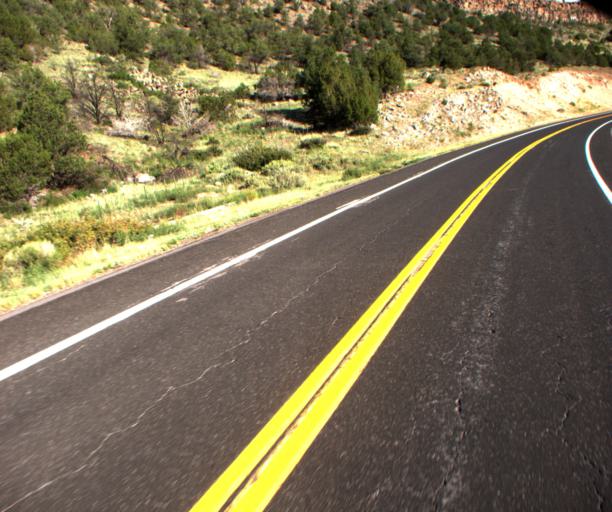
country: US
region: Arizona
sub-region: Apache County
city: Eagar
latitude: 34.0839
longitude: -109.2027
